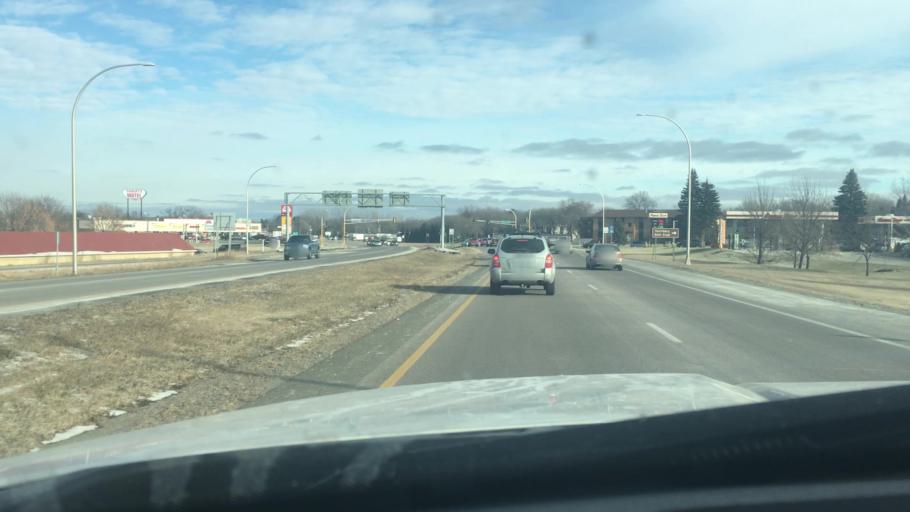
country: US
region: Minnesota
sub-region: Stearns County
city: Saint Cloud
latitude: 45.5671
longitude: -94.1364
